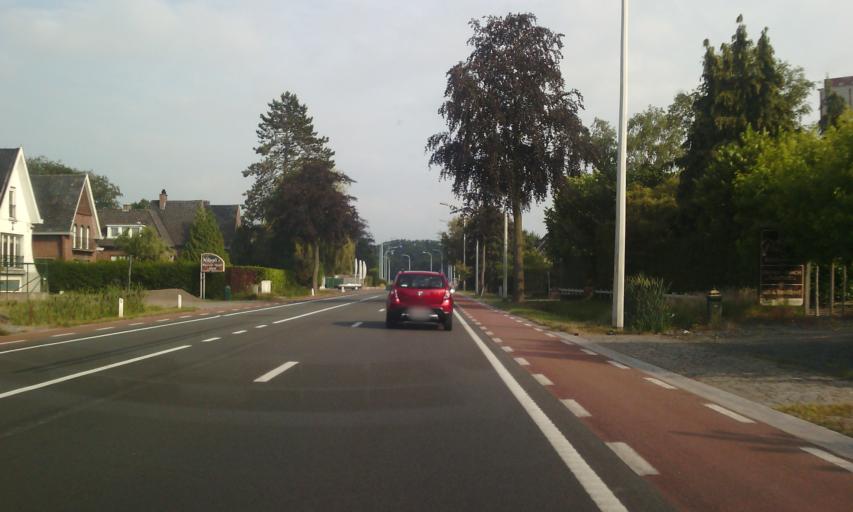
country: BE
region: Flanders
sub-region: Provincie Oost-Vlaanderen
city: Lovendegem
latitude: 51.0949
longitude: 3.6421
